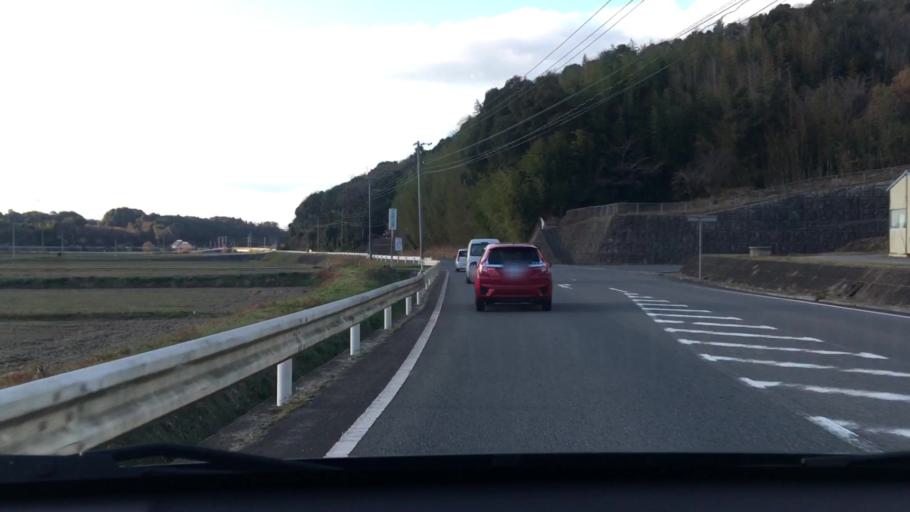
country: JP
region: Oita
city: Bungo-Takada-shi
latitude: 33.5097
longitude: 131.3585
